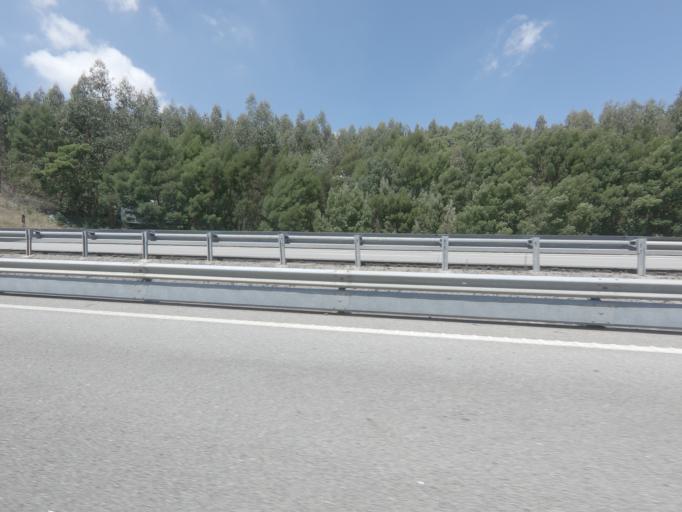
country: PT
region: Porto
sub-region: Paredes
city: Baltar
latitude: 41.1866
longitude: -8.3666
